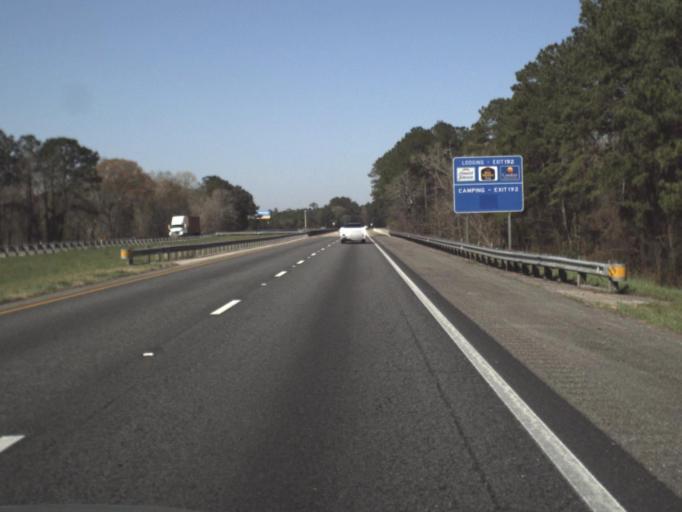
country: US
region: Florida
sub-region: Gadsden County
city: Midway
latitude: 30.4858
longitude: -84.4071
